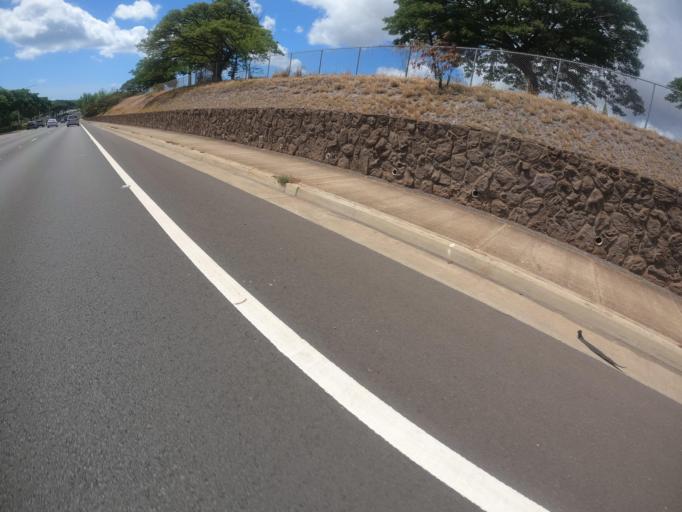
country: US
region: Hawaii
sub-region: Honolulu County
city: Waipahu
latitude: 21.3685
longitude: -158.0264
